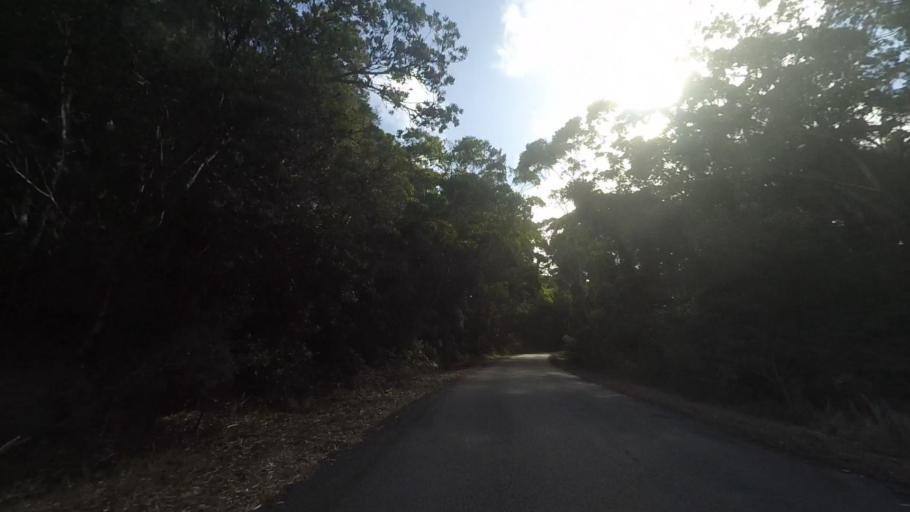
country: AU
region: New South Wales
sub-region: Great Lakes
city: Forster
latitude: -32.4322
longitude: 152.5198
